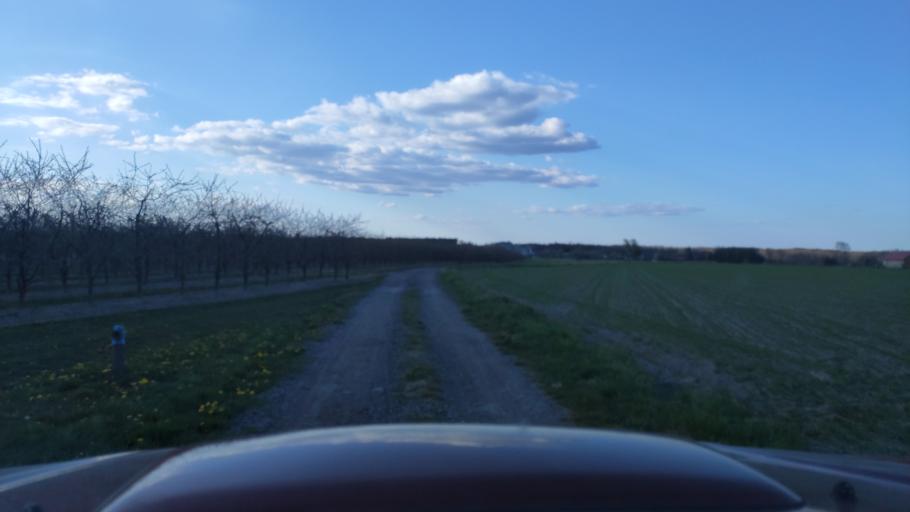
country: PL
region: Masovian Voivodeship
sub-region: Powiat zwolenski
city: Zwolen
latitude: 51.3773
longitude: 21.5753
